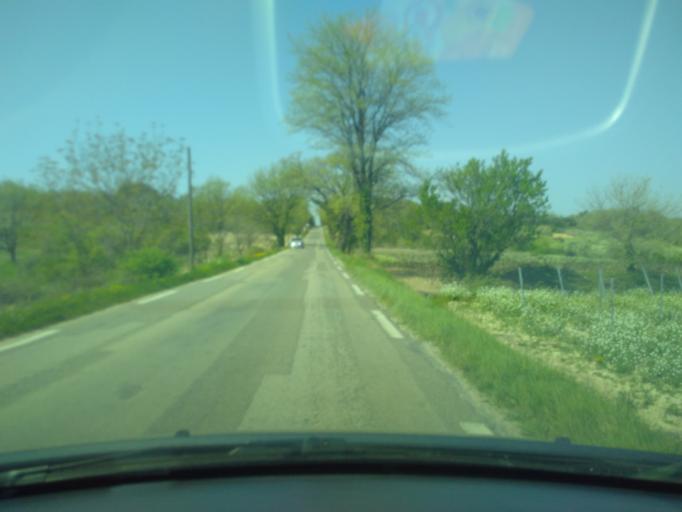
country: FR
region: Provence-Alpes-Cote d'Azur
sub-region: Departement du Vaucluse
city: Malemort-du-Comtat
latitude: 44.0233
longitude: 5.1416
